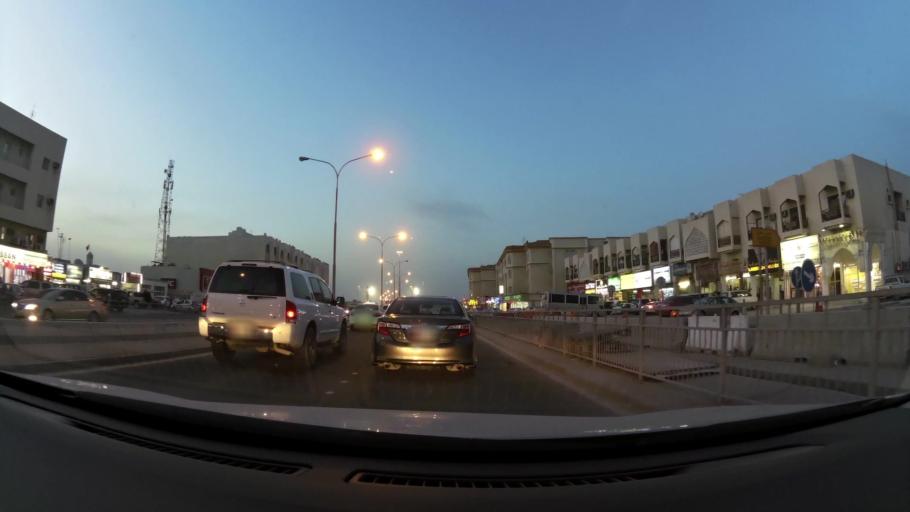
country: QA
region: Al Wakrah
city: Al Wakrah
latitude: 25.1704
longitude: 51.5978
